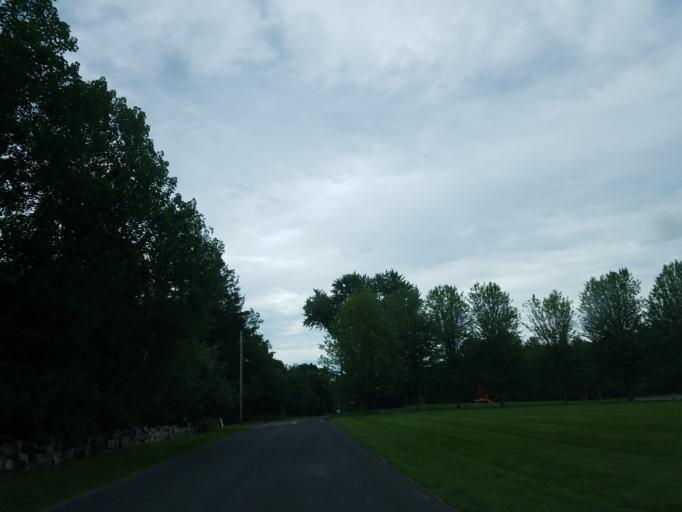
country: US
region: Connecticut
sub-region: Litchfield County
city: West Torrington
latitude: 41.8409
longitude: -73.1589
